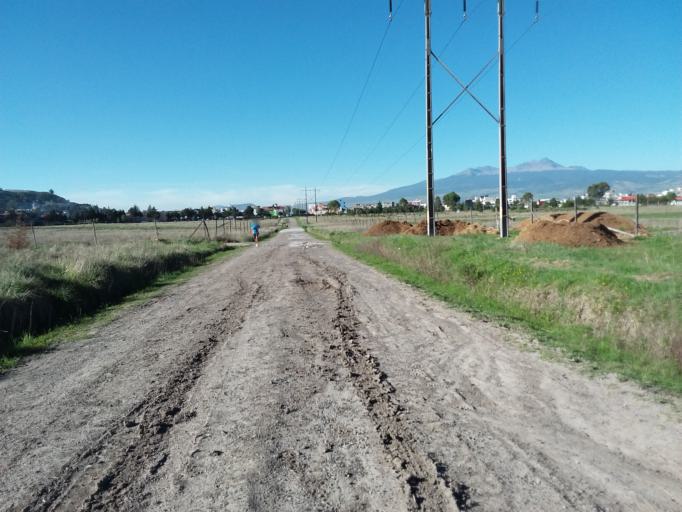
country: MX
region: Mexico
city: San Marcos Yachihuacaltepec
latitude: 19.3096
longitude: -99.6956
